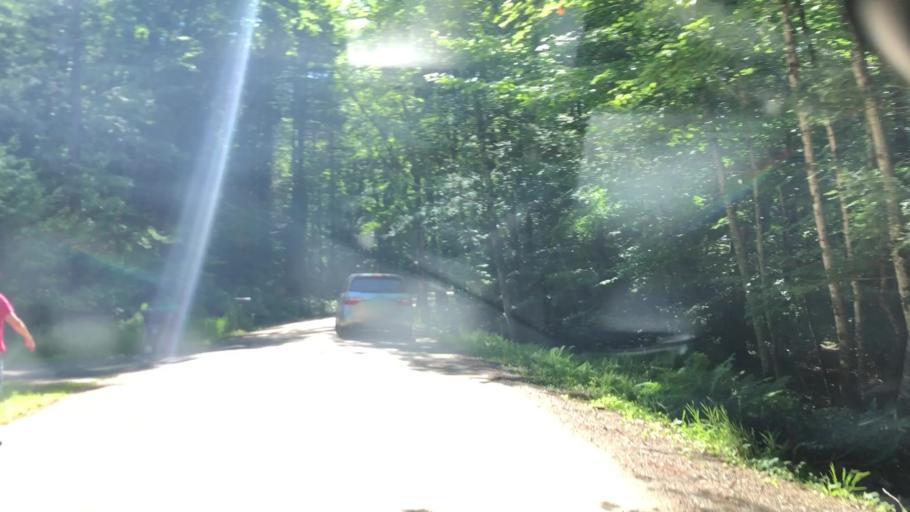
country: US
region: New Hampshire
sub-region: Hillsborough County
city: Mont Vernon
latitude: 42.9175
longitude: -71.6170
